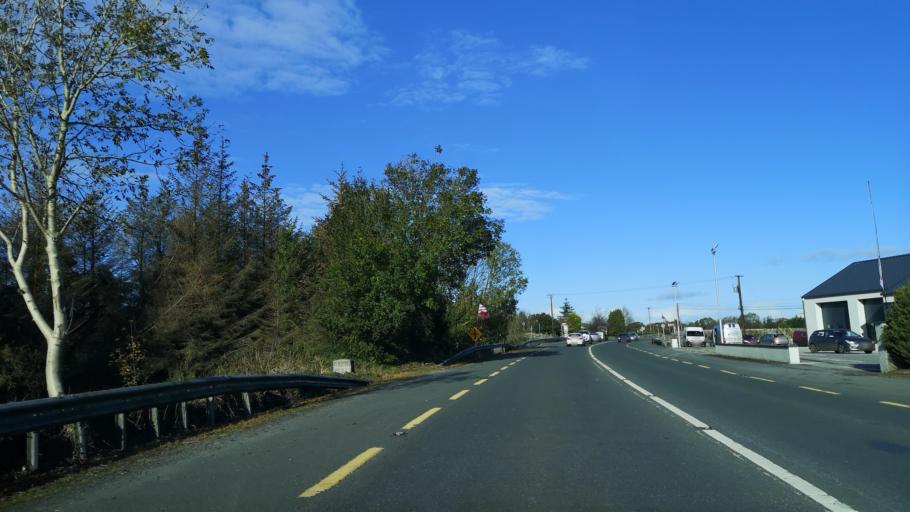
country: IE
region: Connaught
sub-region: County Galway
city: Moycullen
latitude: 53.4514
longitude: -9.0935
